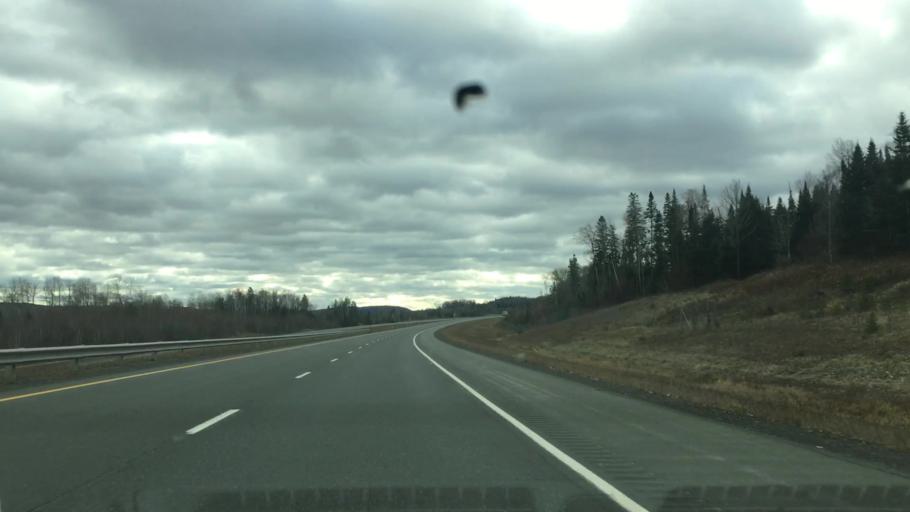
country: US
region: Maine
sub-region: Aroostook County
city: Fort Fairfield
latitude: 46.6768
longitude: -67.7302
